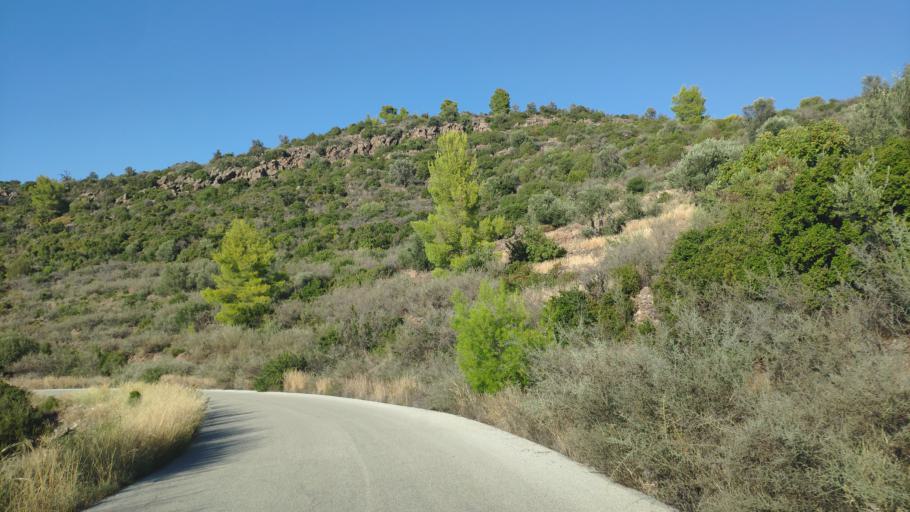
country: GR
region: Attica
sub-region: Nomos Piraios
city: Galatas
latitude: 37.5804
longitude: 23.3524
